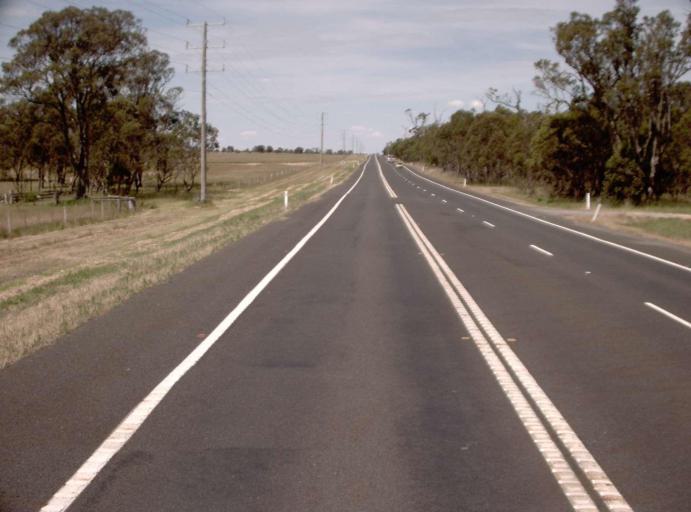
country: AU
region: Victoria
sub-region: East Gippsland
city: Bairnsdale
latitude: -37.8902
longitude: 147.3871
